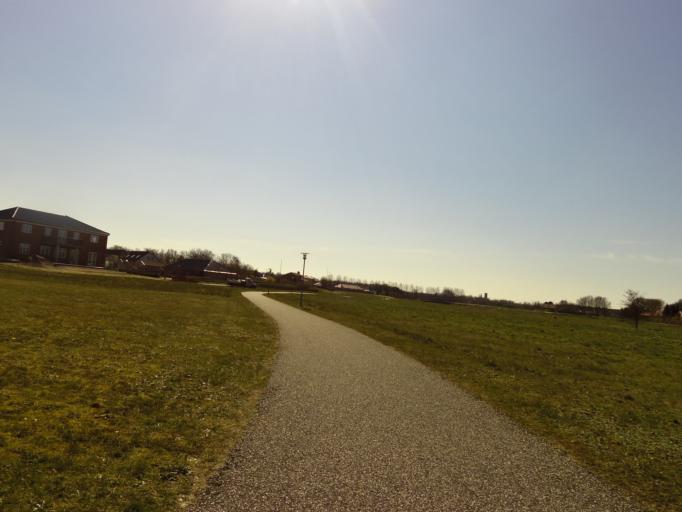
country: DK
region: South Denmark
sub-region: Esbjerg Kommune
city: Ribe
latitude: 55.3395
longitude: 8.7907
